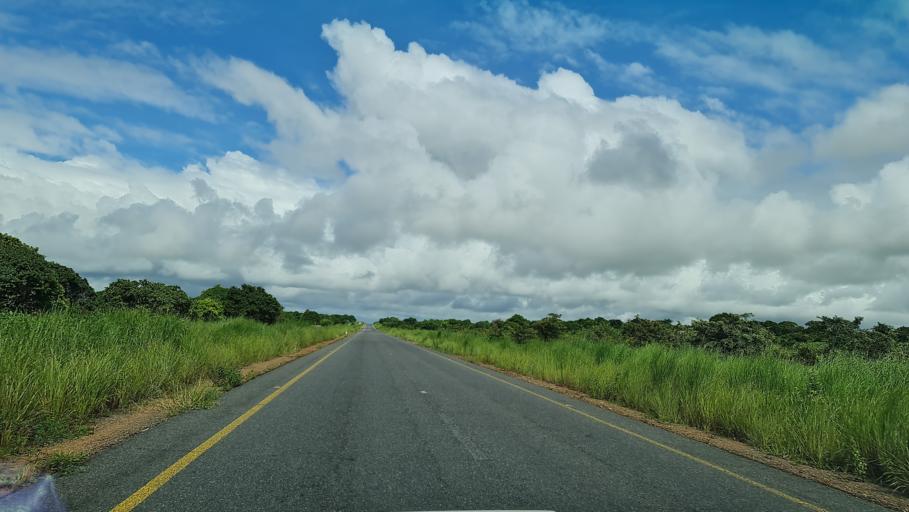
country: MZ
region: Nampula
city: Nampula
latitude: -15.0232
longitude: 38.4838
